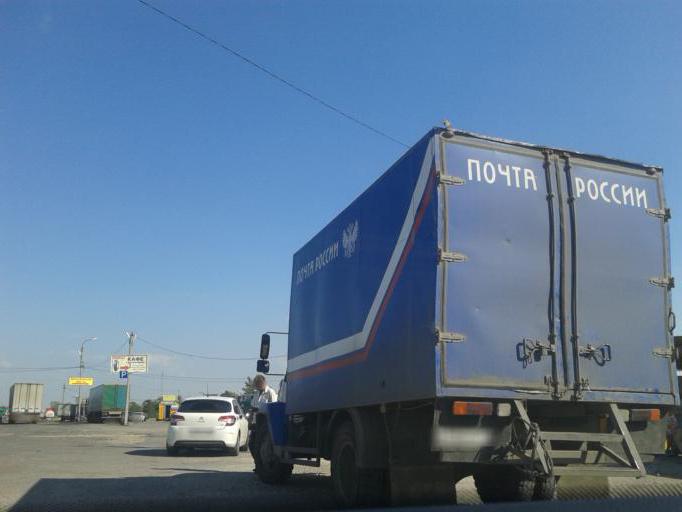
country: RU
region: Volgograd
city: Ilovlya
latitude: 49.3267
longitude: 44.0184
